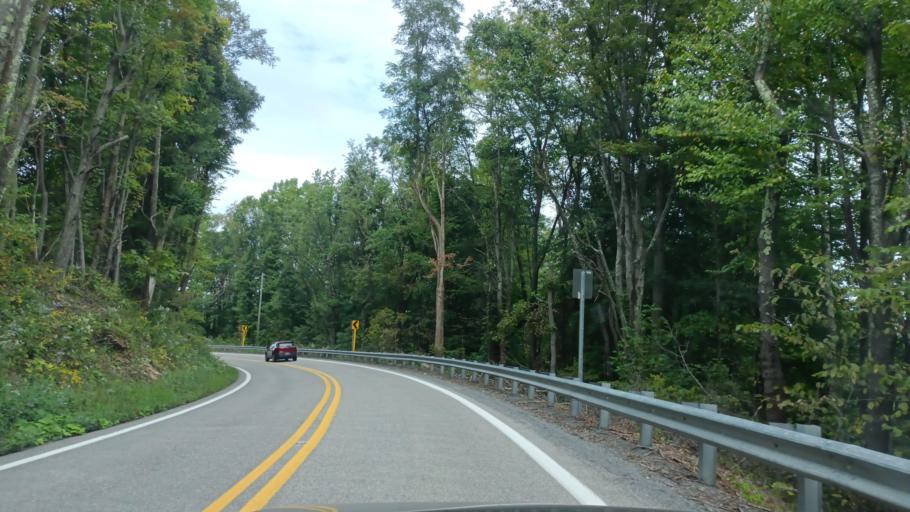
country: US
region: West Virginia
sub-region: Preston County
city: Kingwood
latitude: 39.3316
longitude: -79.7606
